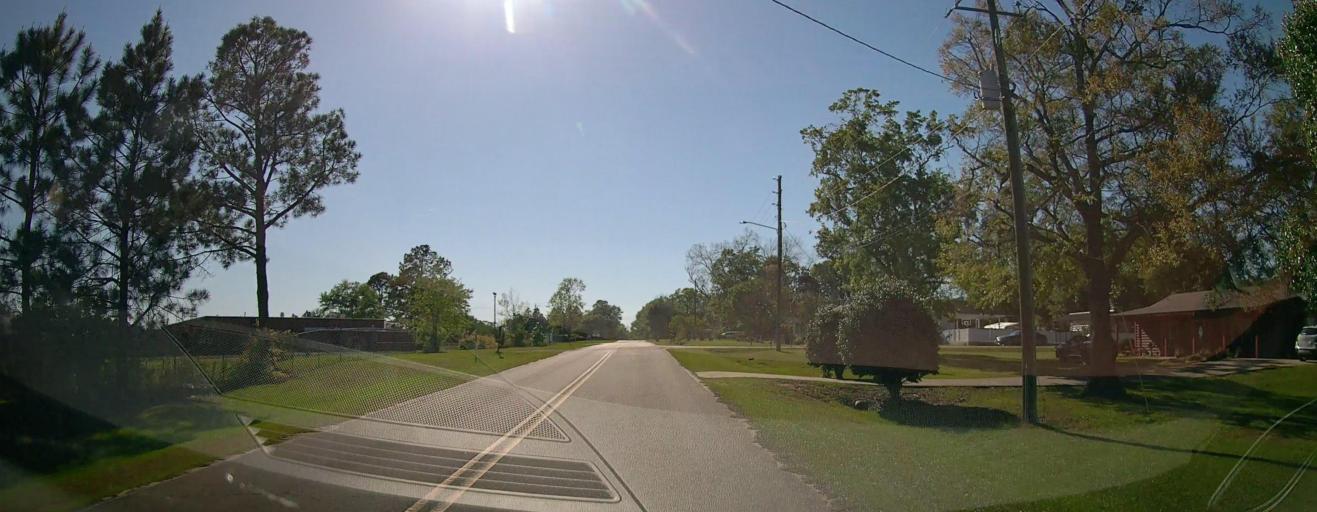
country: US
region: Georgia
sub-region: Wilcox County
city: Rochelle
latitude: 31.9439
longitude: -83.4508
